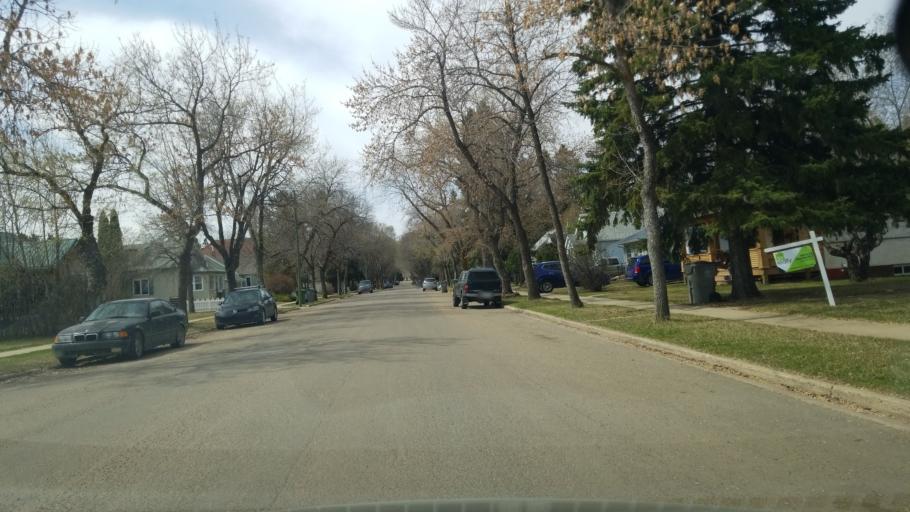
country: CA
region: Saskatchewan
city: Lloydminster
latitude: 53.2825
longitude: -110.0135
